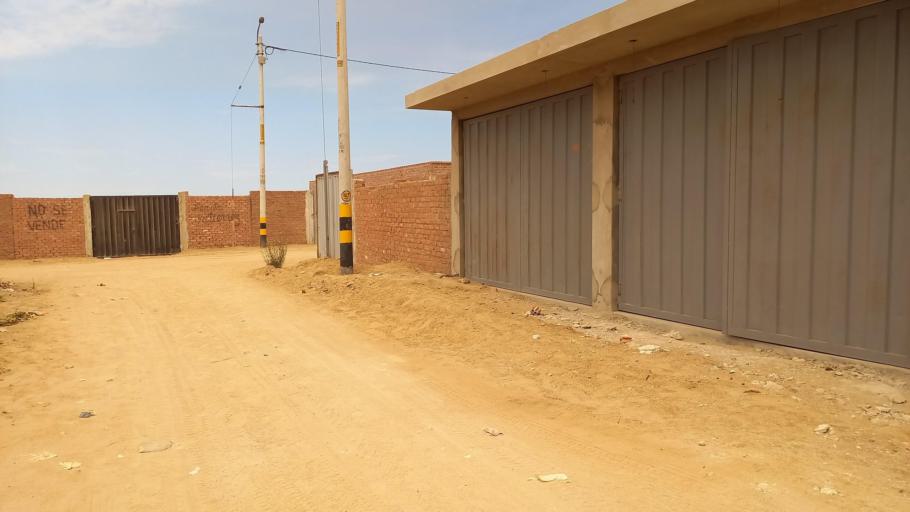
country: PE
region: La Libertad
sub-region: Provincia de Trujillo
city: Trujillo
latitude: -8.1178
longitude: -79.0478
